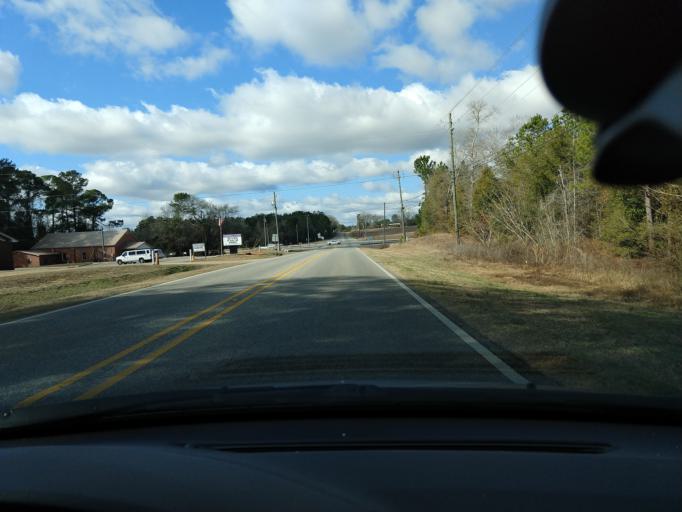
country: US
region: Alabama
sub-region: Coffee County
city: Enterprise
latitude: 31.3241
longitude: -85.8876
